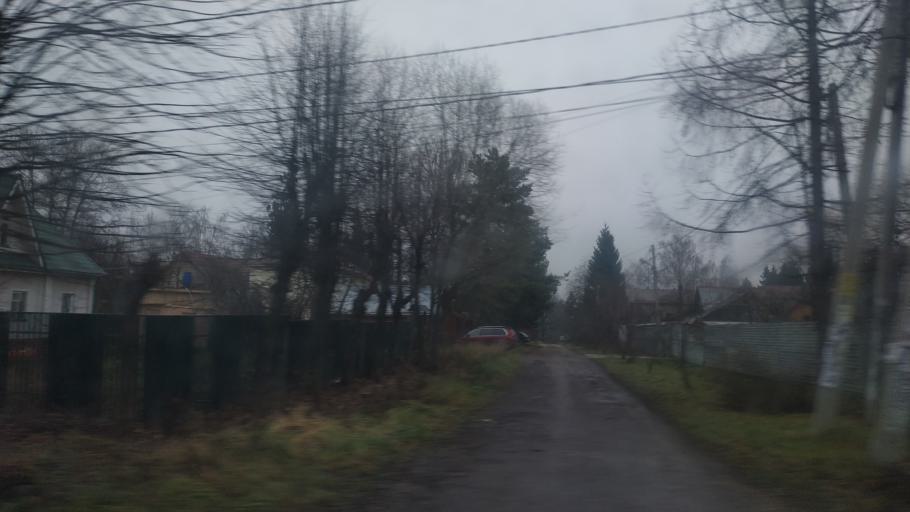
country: RU
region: Moskovskaya
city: Lugovaya
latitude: 56.0529
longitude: 37.4868
